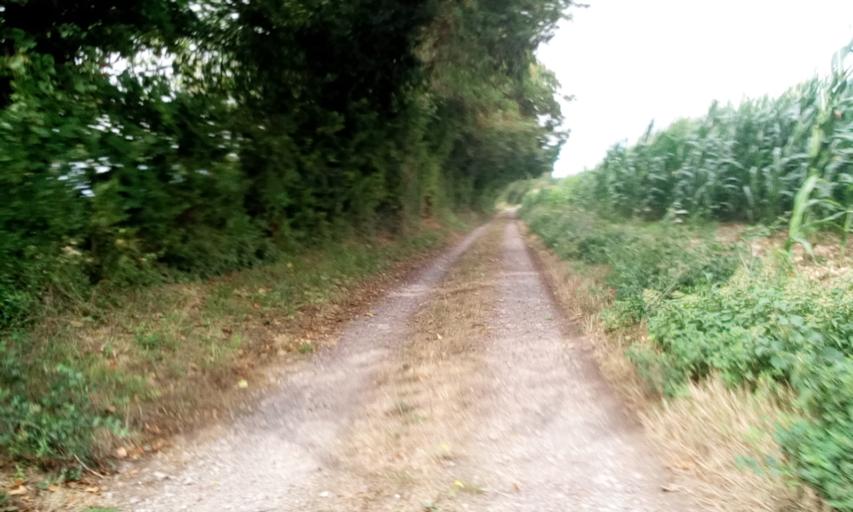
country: FR
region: Lower Normandy
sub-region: Departement du Calvados
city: Tilly-sur-Seulles
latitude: 49.2197
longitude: -0.6240
